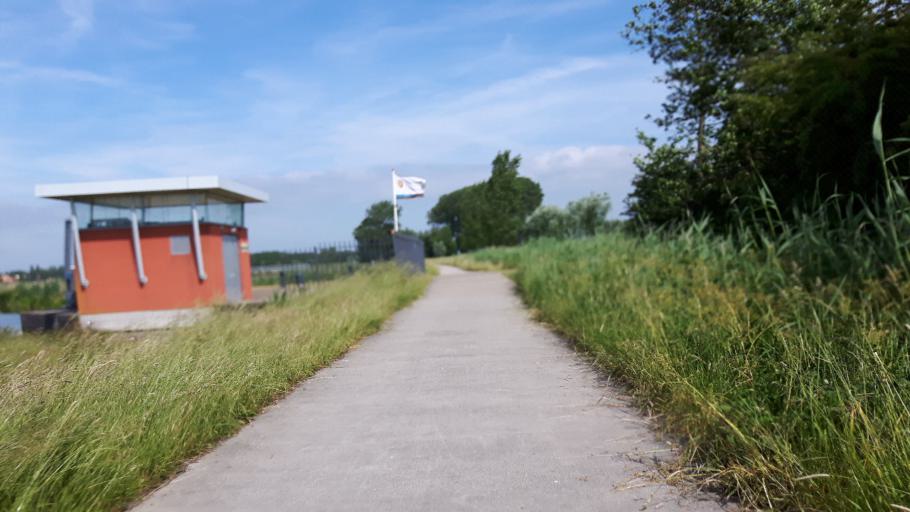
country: NL
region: North Holland
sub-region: Gemeente Uithoorn
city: Uithoorn
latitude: 52.2271
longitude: 4.7976
